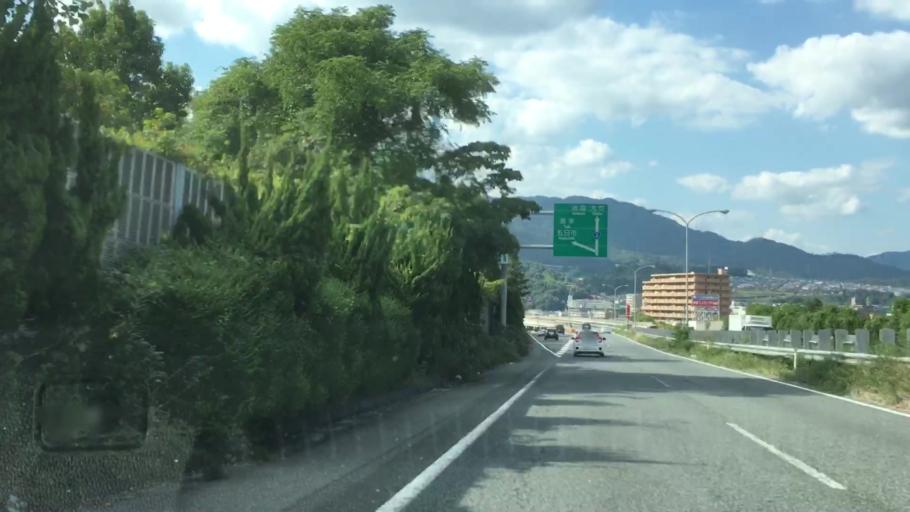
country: JP
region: Hiroshima
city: Hatsukaichi
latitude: 34.3776
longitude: 132.3663
